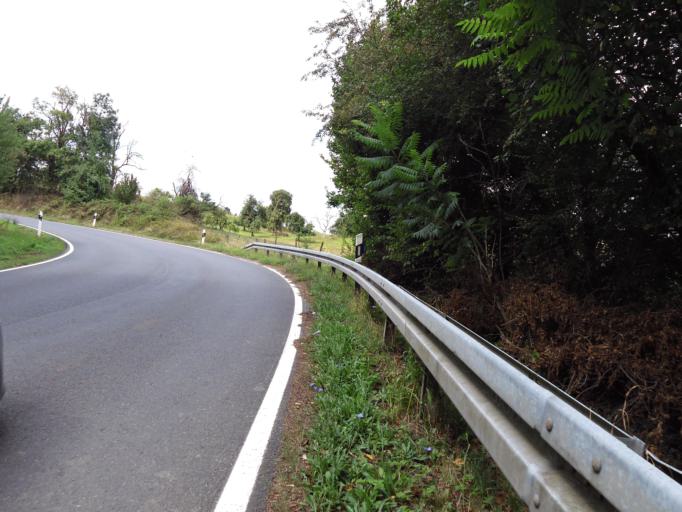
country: DE
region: Hesse
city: Hochst im Odenwald
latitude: 49.7746
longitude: 8.9597
